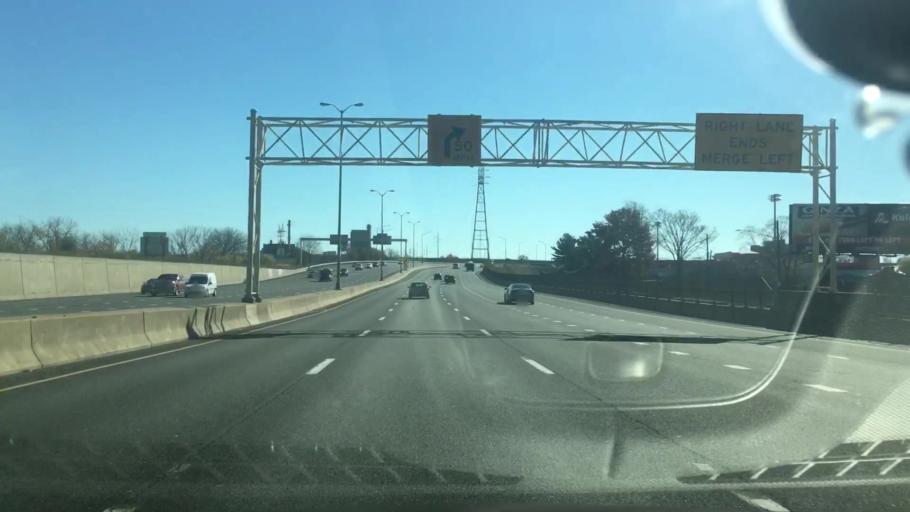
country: US
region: Connecticut
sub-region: Hartford County
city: Hartford
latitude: 41.7562
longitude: -72.6627
